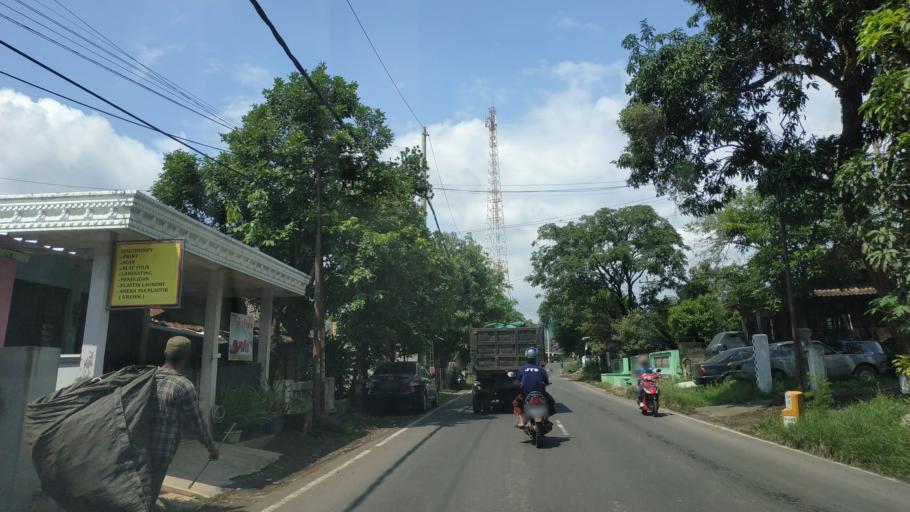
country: ID
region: Central Java
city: Weleri
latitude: -6.9923
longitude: 110.0747
